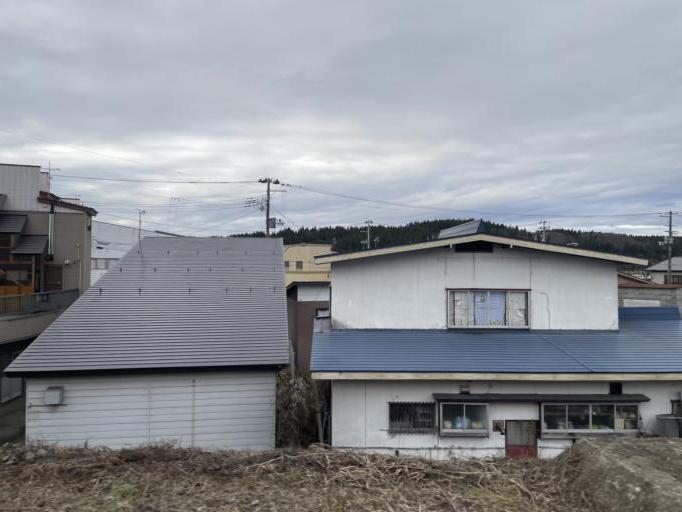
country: JP
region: Yamagata
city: Shinjo
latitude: 38.8603
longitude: 140.2568
